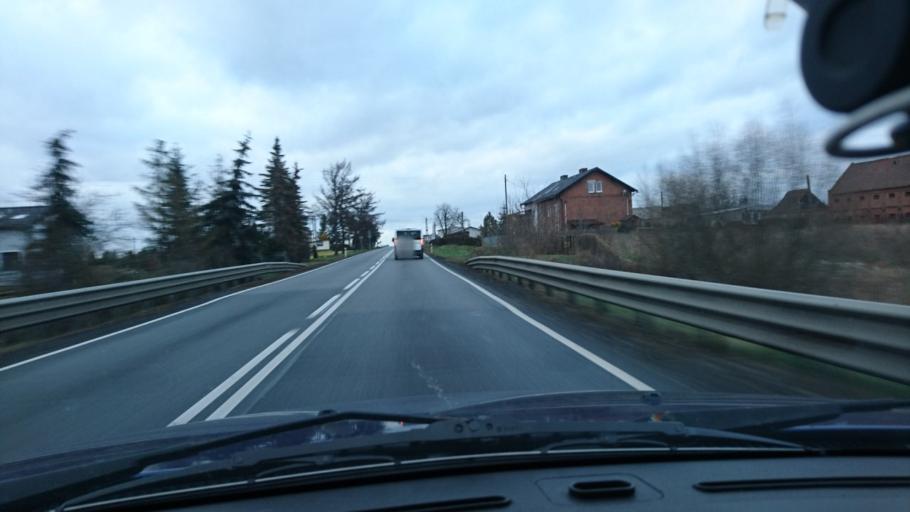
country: PL
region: Opole Voivodeship
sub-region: Powiat kluczborski
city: Kluczbork
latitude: 51.0067
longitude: 18.2047
